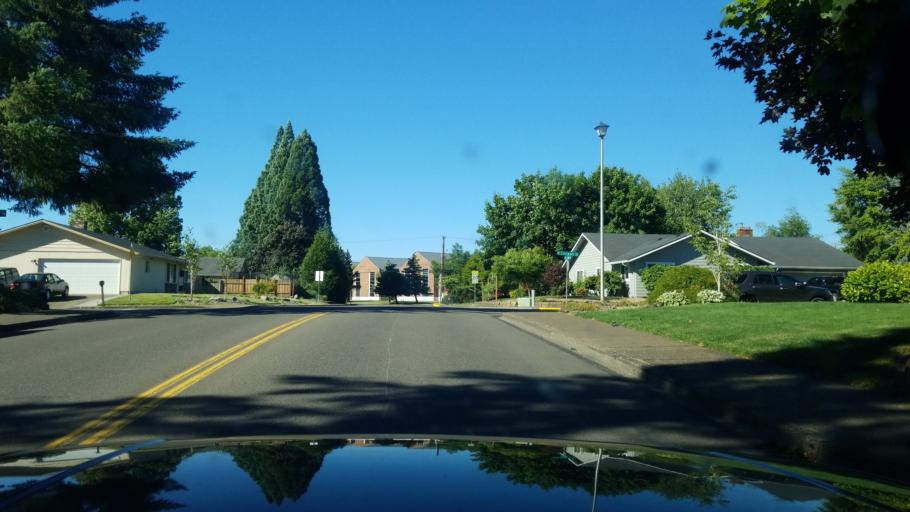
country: US
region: Oregon
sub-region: Yamhill County
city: McMinnville
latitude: 45.2140
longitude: -123.2080
